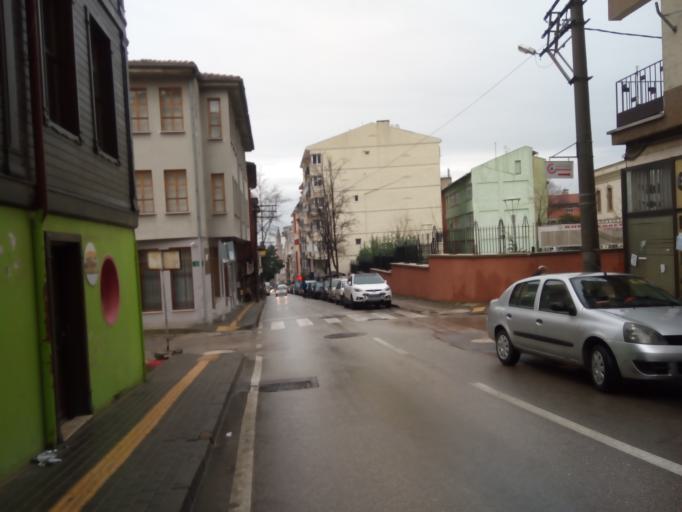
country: TR
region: Bursa
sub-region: Osmangazi
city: Bursa
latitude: 40.1800
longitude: 29.0618
